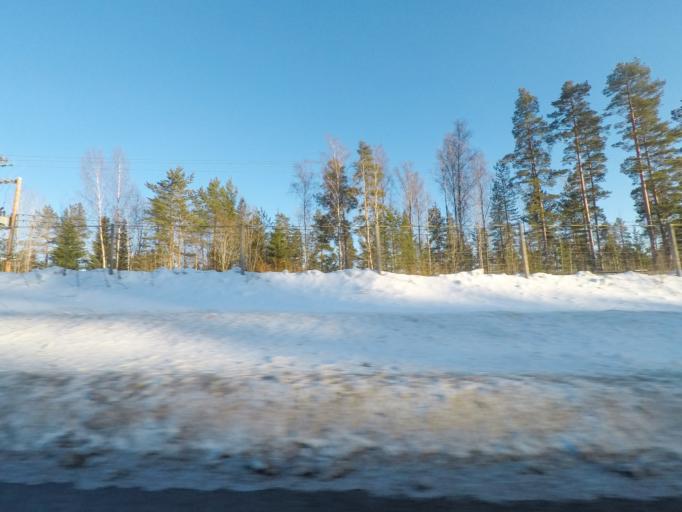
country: FI
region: Southern Savonia
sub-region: Mikkeli
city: Pertunmaa
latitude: 61.3710
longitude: 26.2896
